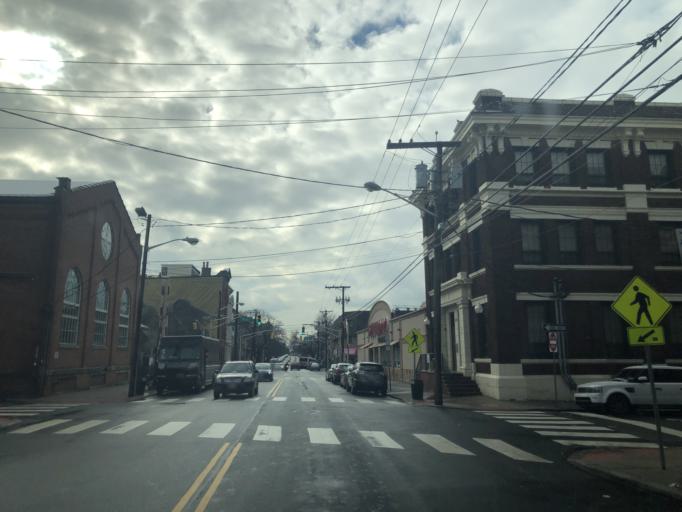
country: US
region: New Jersey
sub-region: Hudson County
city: Hoboken
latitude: 40.7401
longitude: -74.0469
